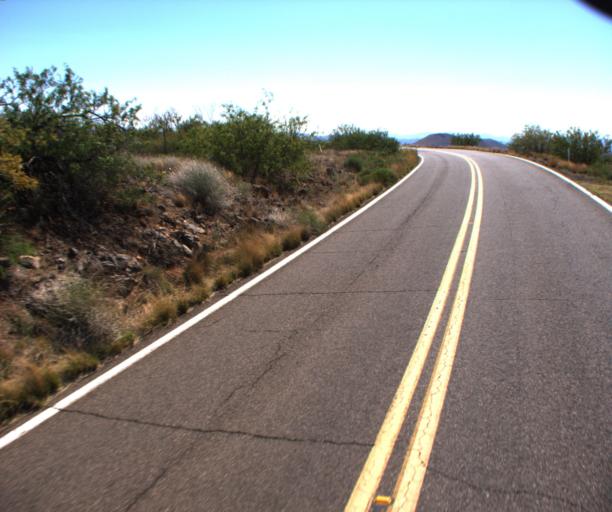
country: US
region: Arizona
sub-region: Cochise County
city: Douglas
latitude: 31.4596
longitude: -109.3783
